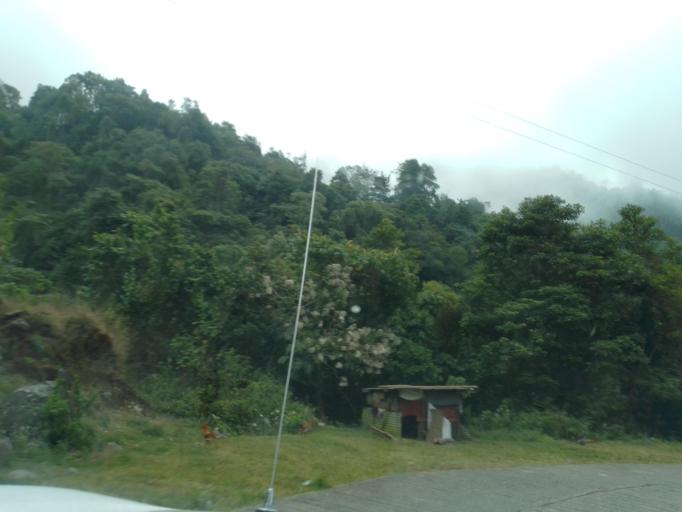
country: MX
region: Chiapas
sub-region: Union Juarez
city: Santo Domingo
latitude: 15.0933
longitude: -92.0946
